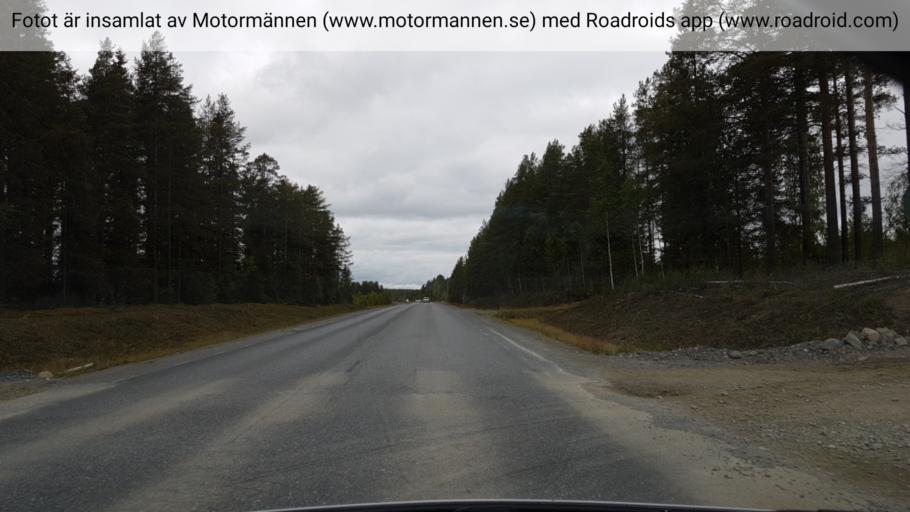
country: SE
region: Vaesterbotten
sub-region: Skelleftea Kommun
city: Boliden
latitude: 64.8818
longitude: 20.3070
